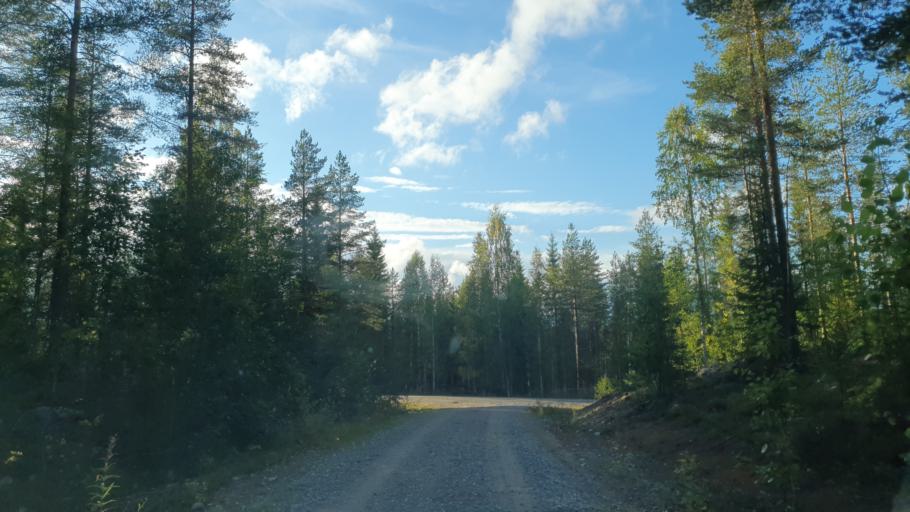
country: FI
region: Kainuu
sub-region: Kehys-Kainuu
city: Kuhmo
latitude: 64.3400
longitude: 29.9786
